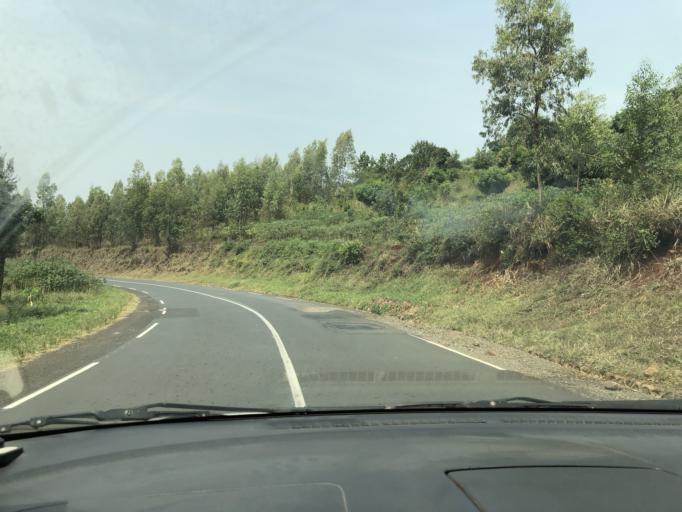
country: RW
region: Western Province
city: Cyangugu
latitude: -2.6696
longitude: 29.0020
